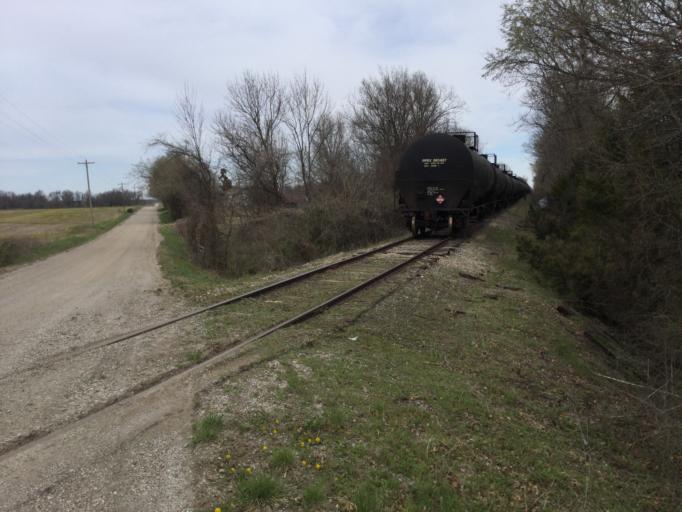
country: US
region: Kansas
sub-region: Cherokee County
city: Columbus
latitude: 37.1662
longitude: -94.9590
